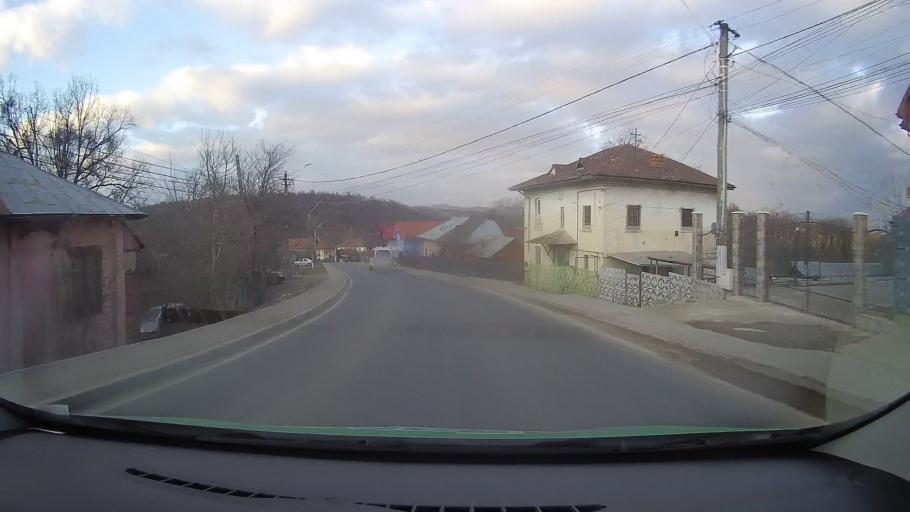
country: RO
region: Dambovita
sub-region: Municipiul Moreni
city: Moreni
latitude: 44.9730
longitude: 25.6160
